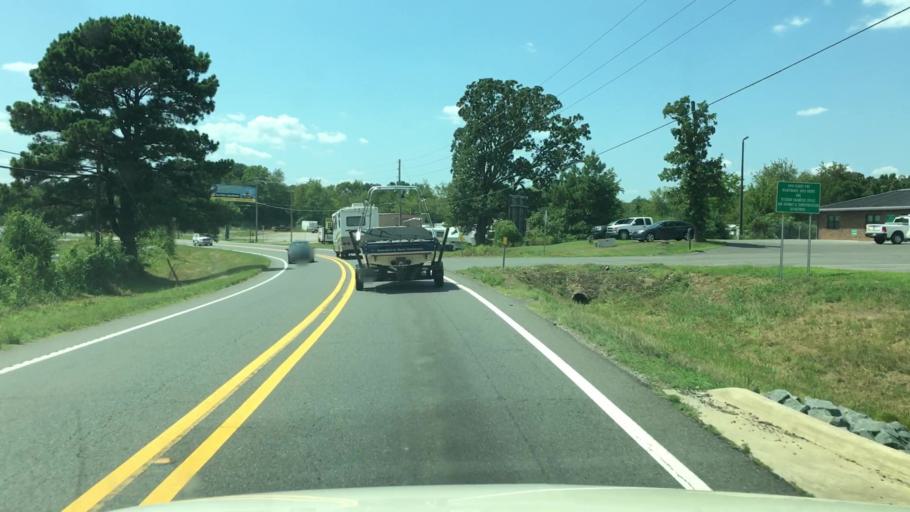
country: US
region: Arkansas
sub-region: Garland County
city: Piney
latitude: 34.5090
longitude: -93.1414
